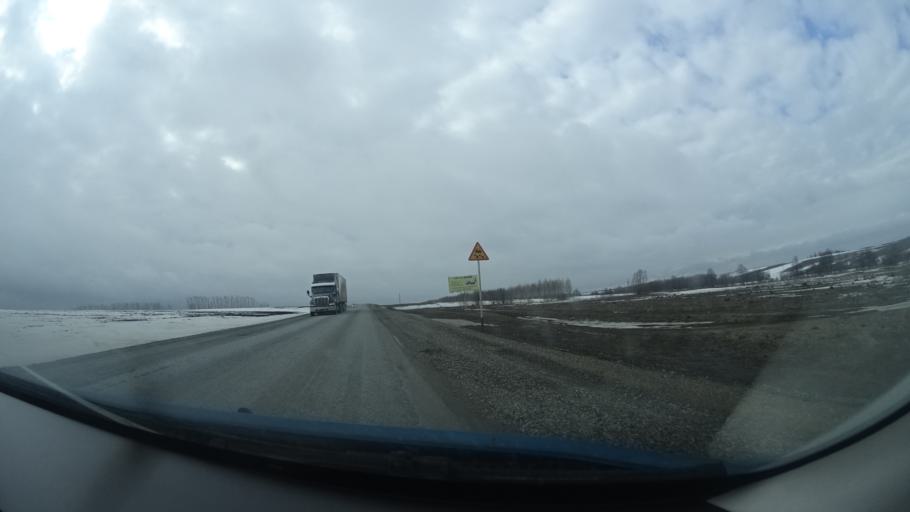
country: RU
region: Bashkortostan
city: Birsk
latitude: 55.3950
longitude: 55.5851
